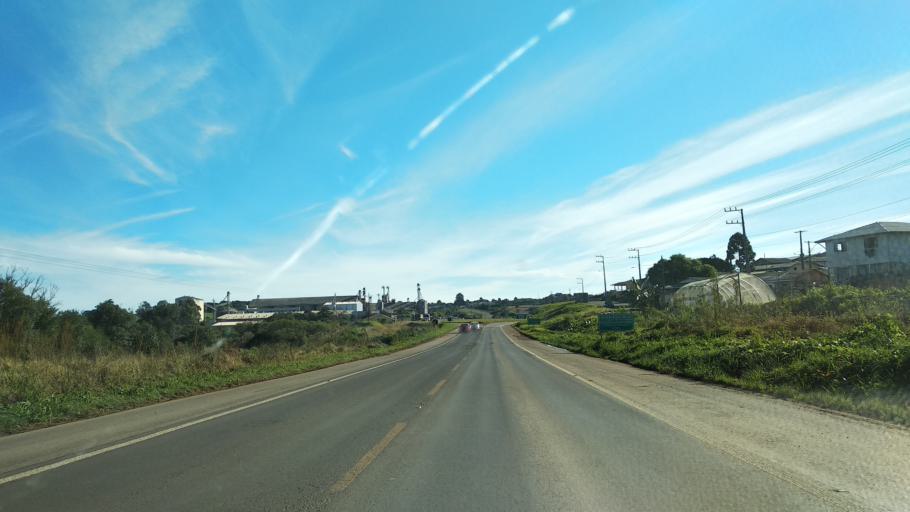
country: BR
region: Santa Catarina
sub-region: Campos Novos
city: Campos Novos
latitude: -27.4080
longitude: -51.2116
